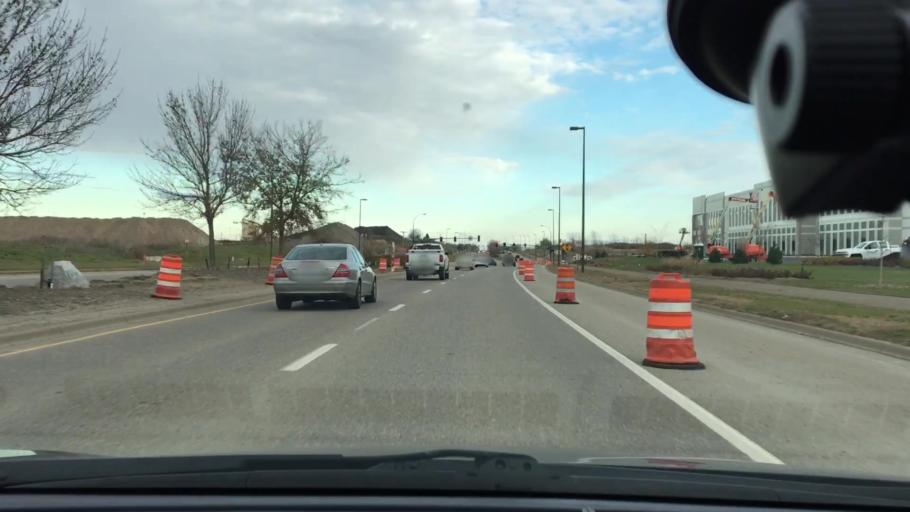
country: US
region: Minnesota
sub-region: Hennepin County
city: Osseo
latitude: 45.0947
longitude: -93.4152
